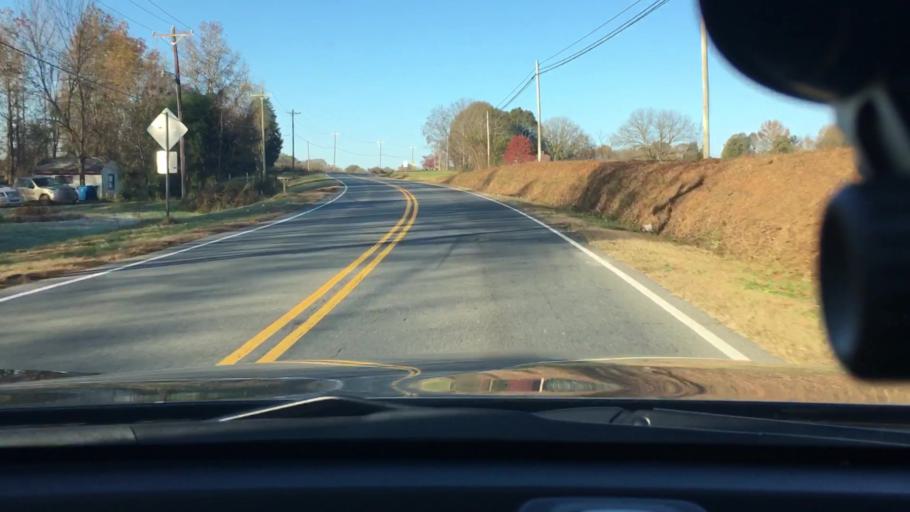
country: US
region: North Carolina
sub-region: Cabarrus County
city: Mount Pleasant
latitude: 35.3961
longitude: -80.4178
